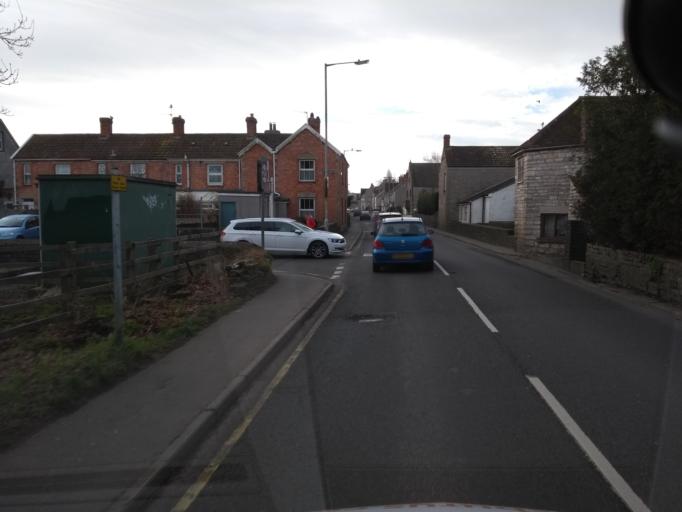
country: GB
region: England
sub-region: Somerset
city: Street
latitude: 51.1324
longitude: -2.7358
